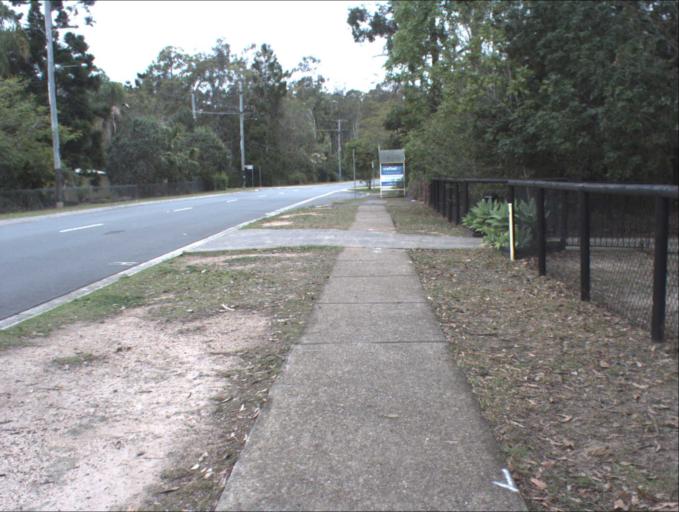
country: AU
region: Queensland
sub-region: Brisbane
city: Forest Lake
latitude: -27.6579
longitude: 153.0074
